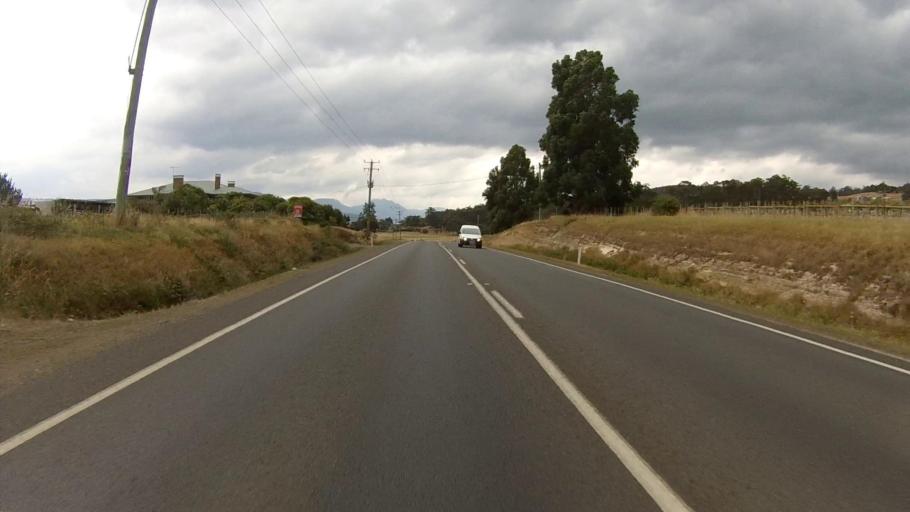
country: AU
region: Tasmania
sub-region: Huon Valley
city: Huonville
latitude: -43.0111
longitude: 147.0646
